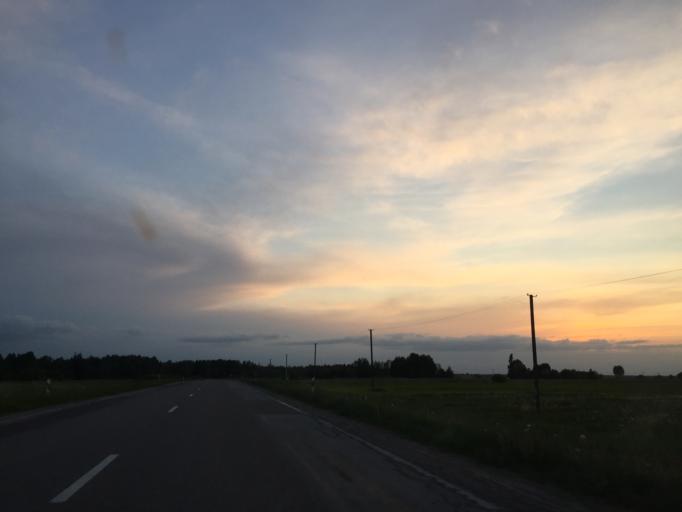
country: LT
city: Venta
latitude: 56.0058
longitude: 22.7113
